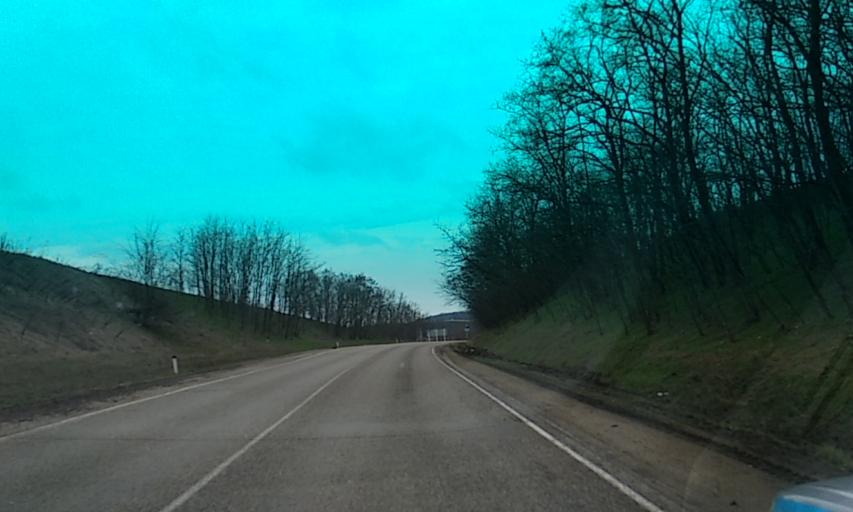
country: RU
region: Krasnodarskiy
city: Vyselki
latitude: 45.4453
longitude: 39.7085
